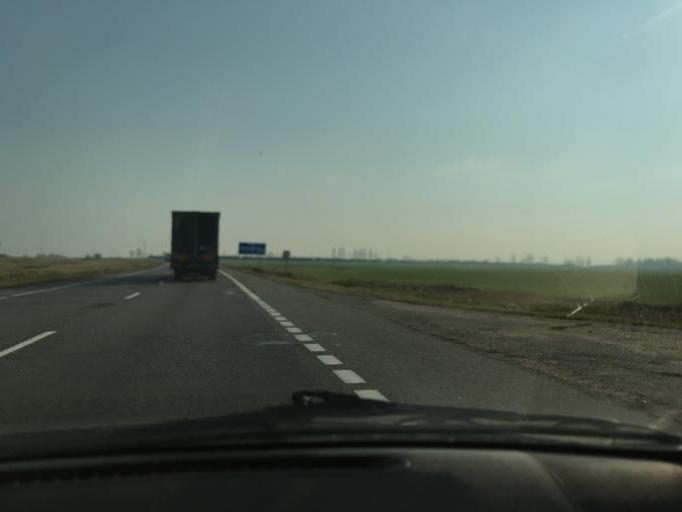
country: BY
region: Vitebsk
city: Chashniki
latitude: 55.0079
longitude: 29.1327
